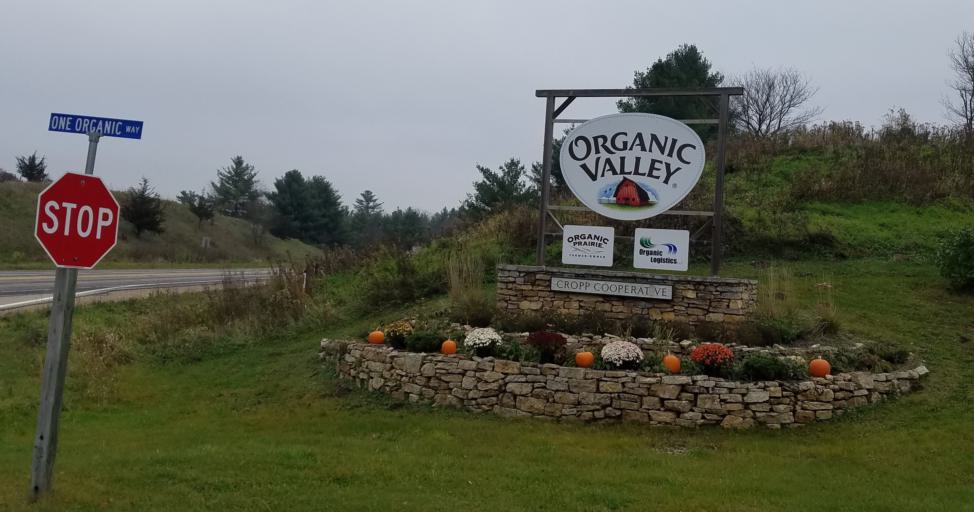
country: US
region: Wisconsin
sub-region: Monroe County
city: Cashton
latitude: 43.5742
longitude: -90.6387
